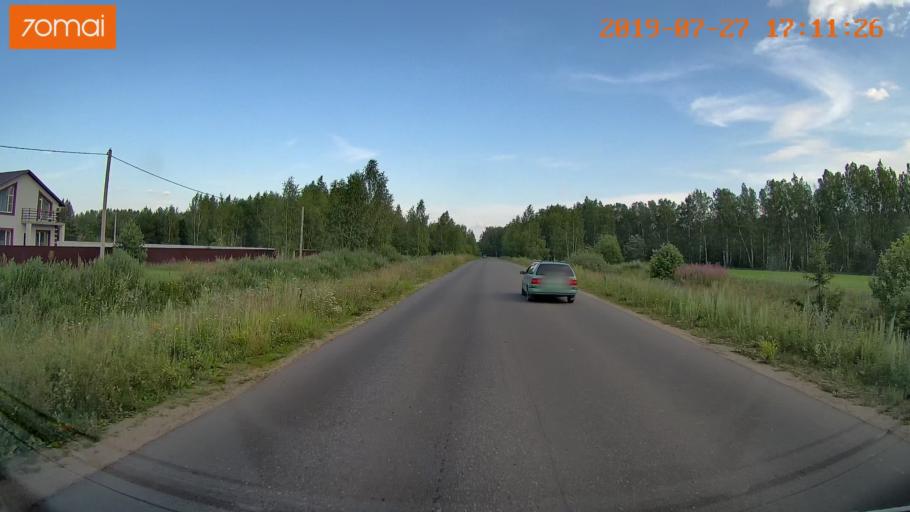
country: RU
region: Ivanovo
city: Novo-Talitsy
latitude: 57.0647
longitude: 40.8616
